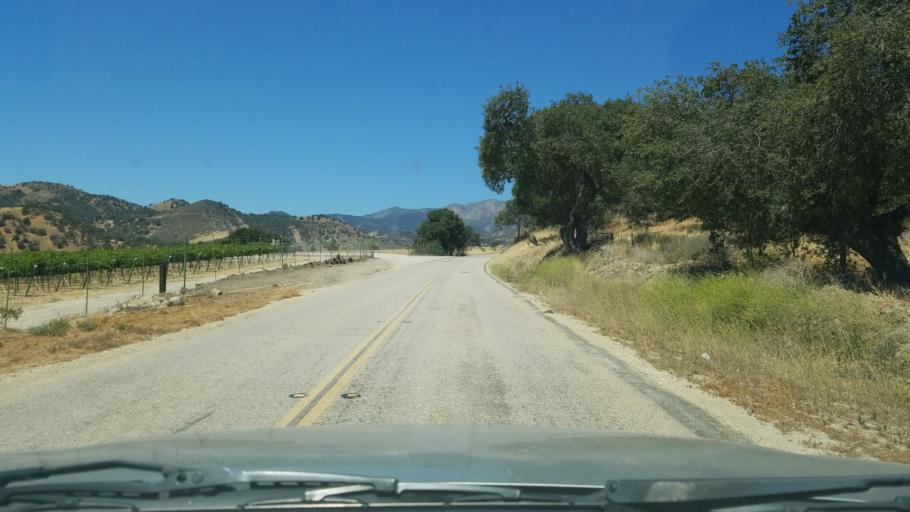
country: US
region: California
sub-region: Monterey County
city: Greenfield
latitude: 36.2677
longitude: -121.3731
